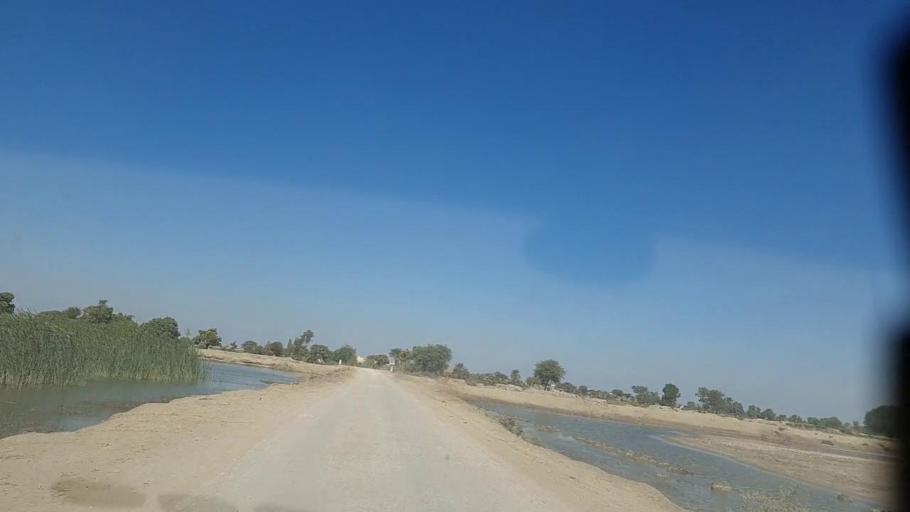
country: PK
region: Sindh
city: Digri
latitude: 25.1773
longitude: 69.0486
